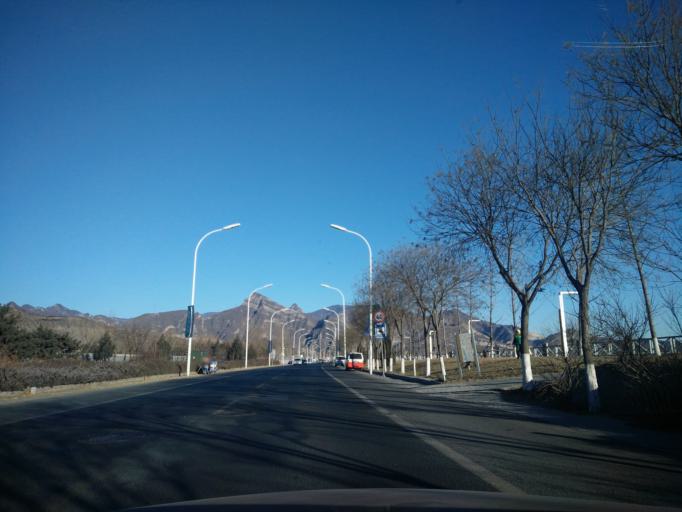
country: CN
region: Beijing
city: Junzhuang
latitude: 39.9784
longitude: 116.0836
